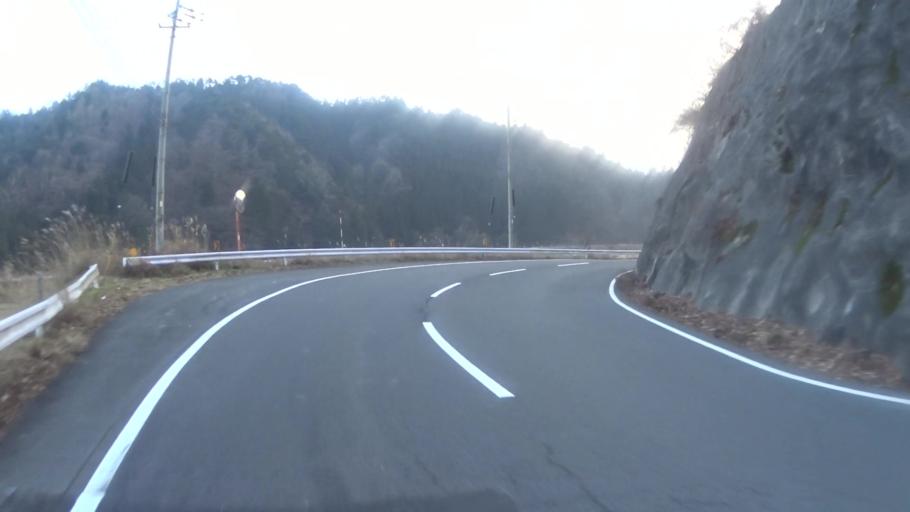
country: JP
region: Kyoto
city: Maizuru
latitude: 35.3809
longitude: 135.4481
